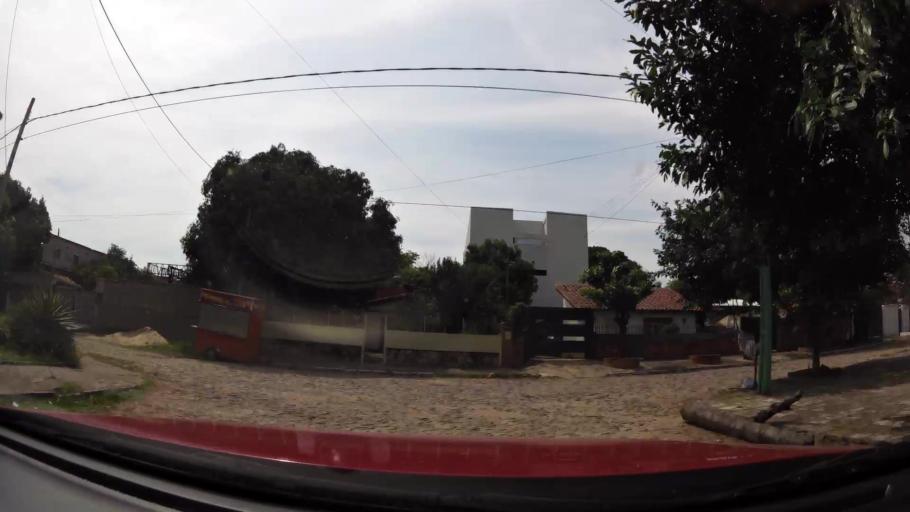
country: PY
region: Asuncion
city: Asuncion
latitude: -25.2627
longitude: -57.5829
